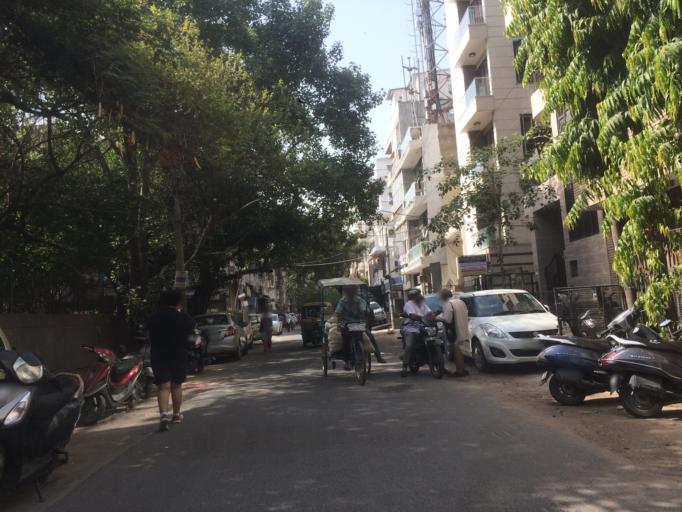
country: IN
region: NCT
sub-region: New Delhi
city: New Delhi
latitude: 28.5622
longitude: 77.2477
